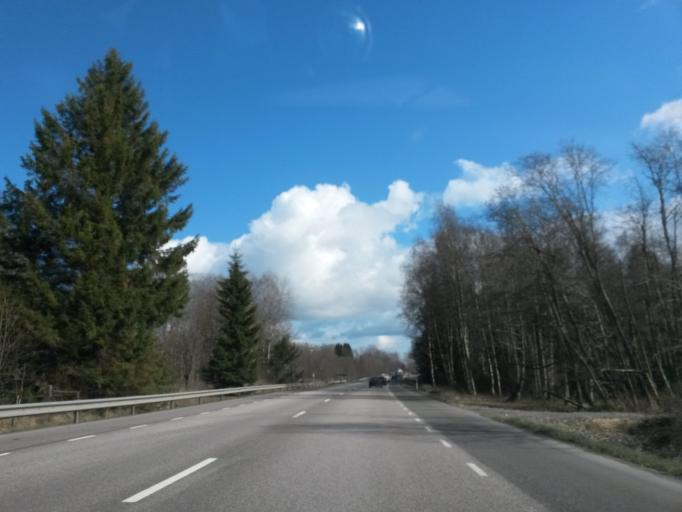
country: SE
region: Vaestra Goetaland
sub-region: Skovde Kommun
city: Skoevde
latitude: 58.3918
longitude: 13.7834
